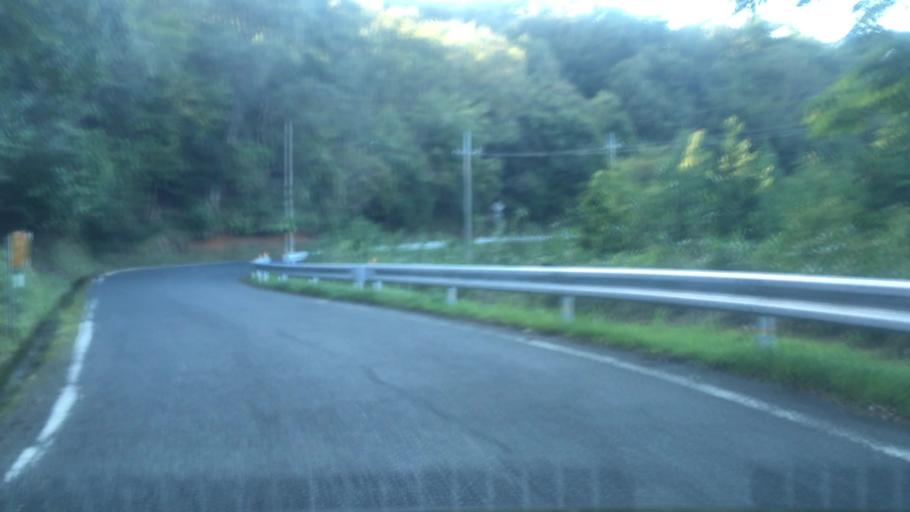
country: JP
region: Hyogo
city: Toyooka
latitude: 35.6176
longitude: 134.8743
